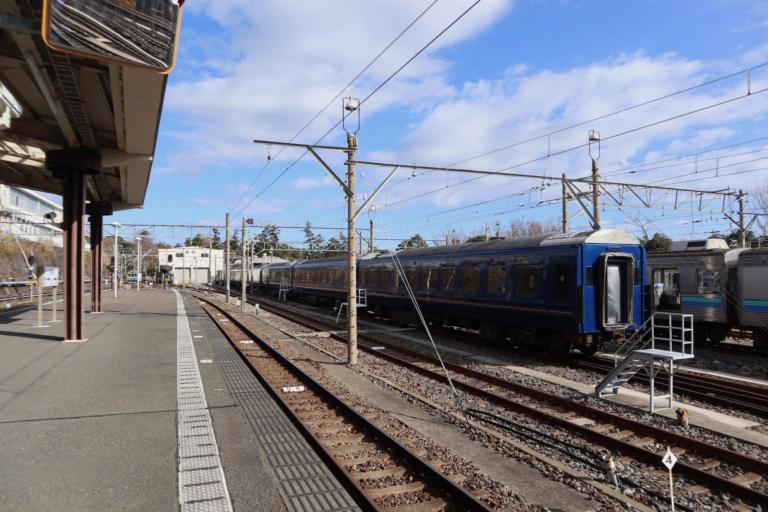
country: JP
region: Shizuoka
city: Ito
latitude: 34.8781
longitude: 139.1087
